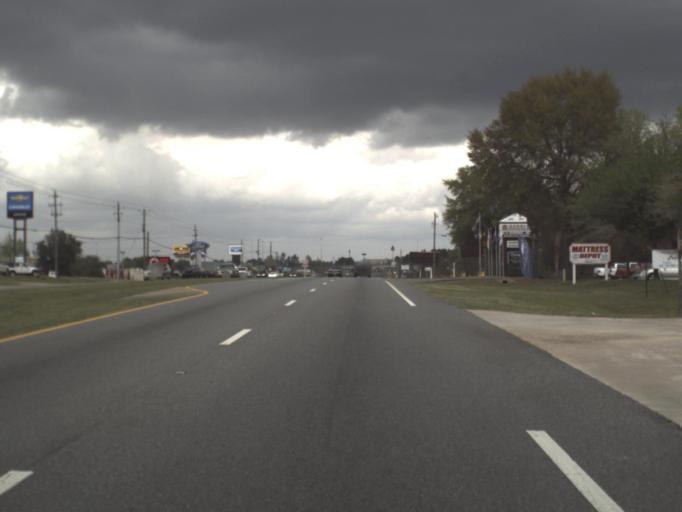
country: US
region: Florida
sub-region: Okaloosa County
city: Crestview
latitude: 30.7157
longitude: -86.5697
